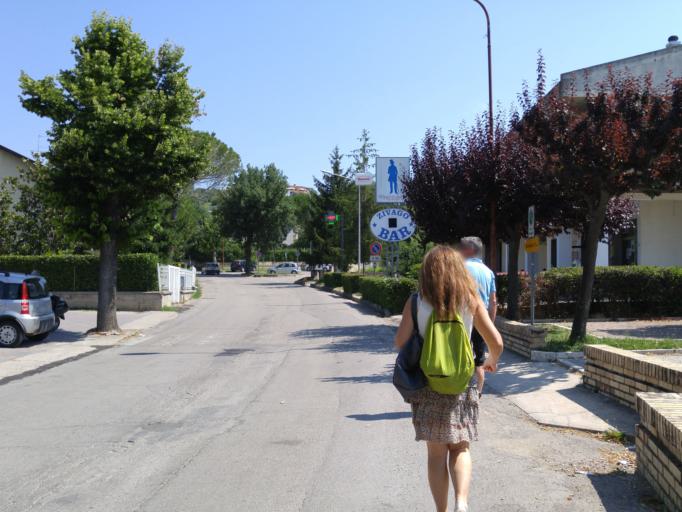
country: IT
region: Abruzzo
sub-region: Provincia di Teramo
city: Castilenti
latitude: 42.5345
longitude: 13.9197
